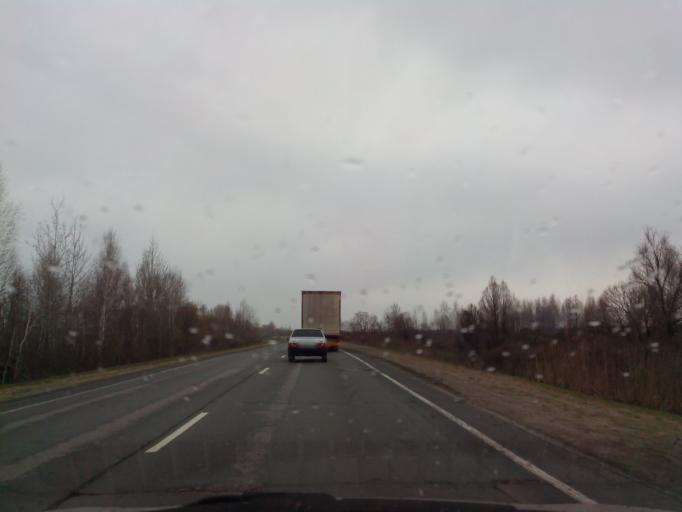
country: RU
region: Tambov
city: Pervomayskiy
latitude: 53.1110
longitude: 40.3924
